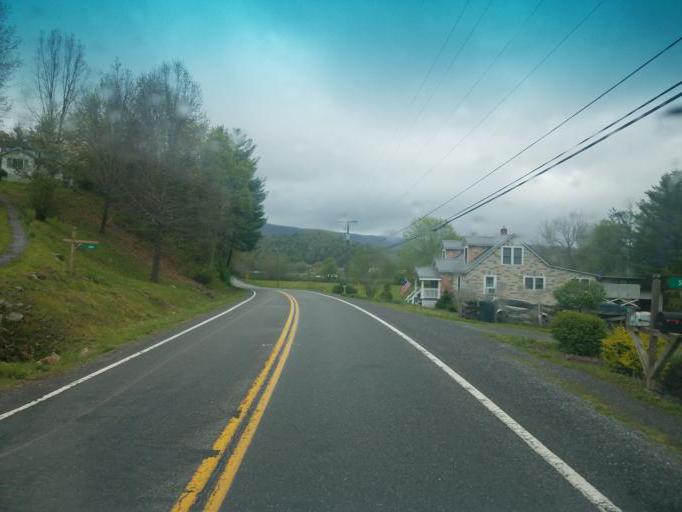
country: US
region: Virginia
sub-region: Bland County
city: Bland
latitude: 37.1679
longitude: -81.1458
